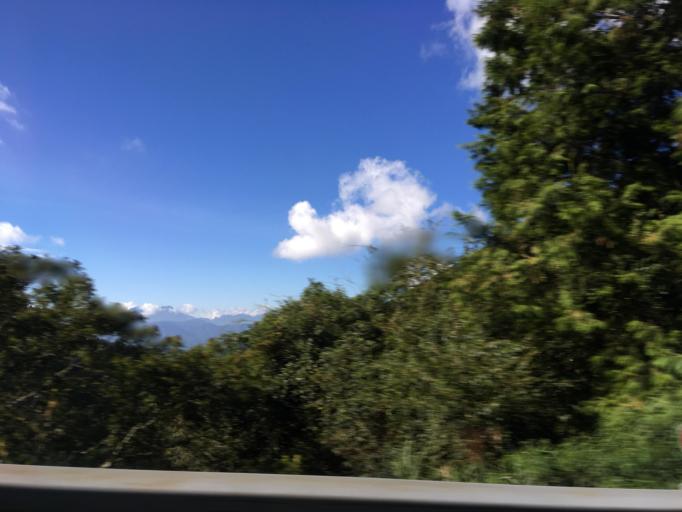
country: TW
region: Taiwan
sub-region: Yilan
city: Yilan
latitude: 24.5162
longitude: 121.5722
